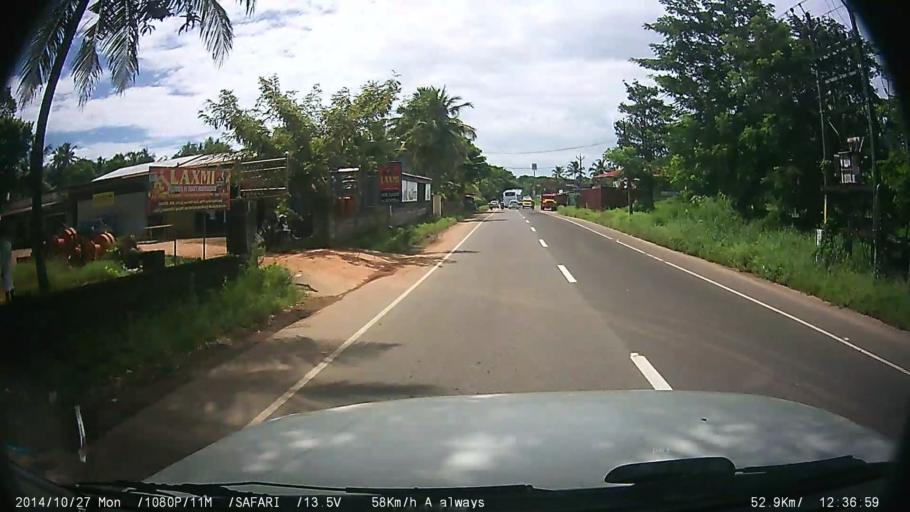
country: IN
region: Kerala
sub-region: Kottayam
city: Changanacheri
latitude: 9.4361
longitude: 76.5387
